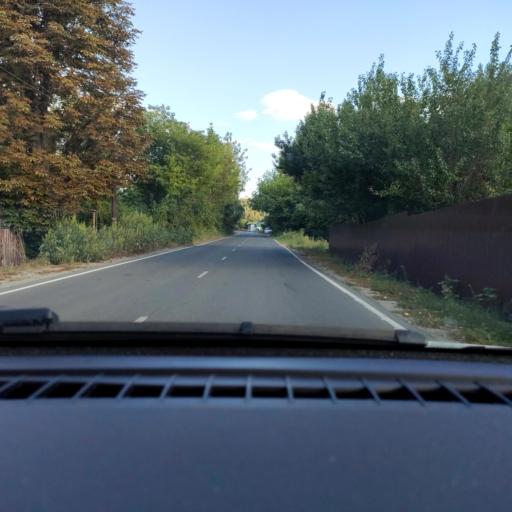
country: RU
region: Voronezj
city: Devitsa
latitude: 51.6563
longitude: 38.9773
